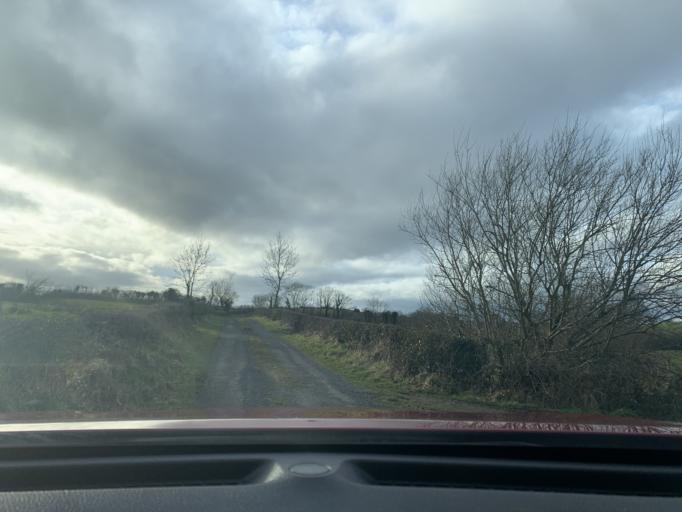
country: IE
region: Connaught
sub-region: Sligo
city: Ballymote
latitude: 54.0239
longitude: -8.5133
